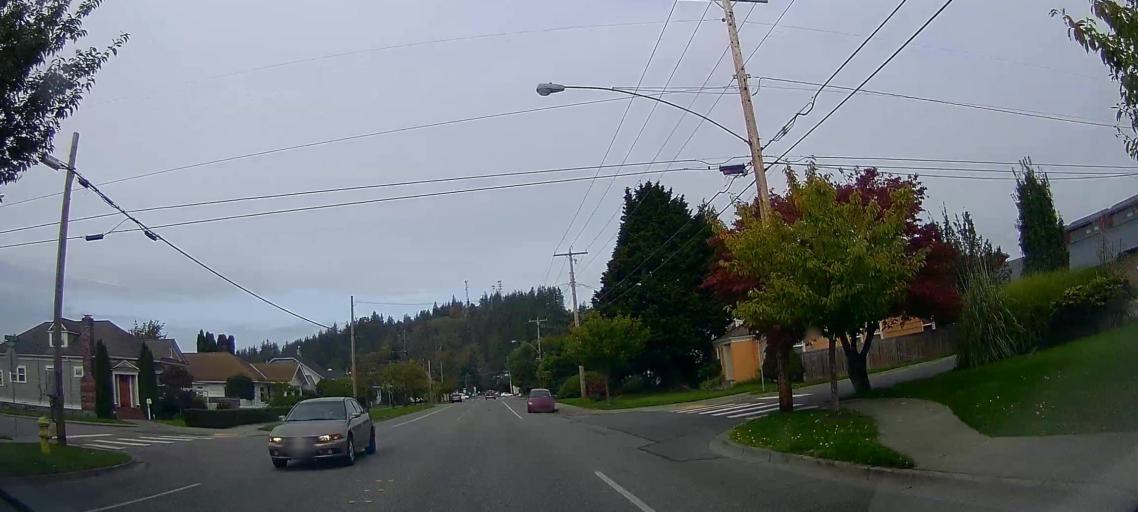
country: US
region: Washington
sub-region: Skagit County
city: Burlington
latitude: 48.4738
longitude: -122.3248
